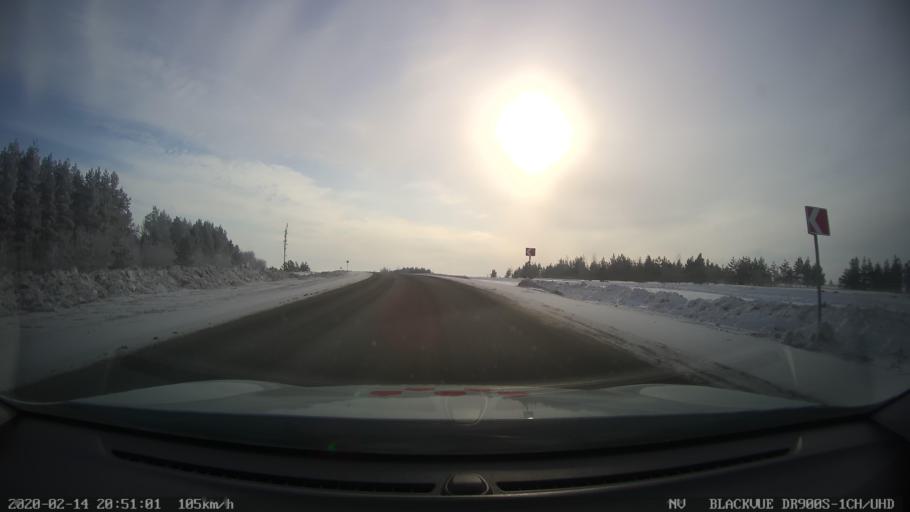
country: RU
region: Tatarstan
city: Kuybyshevskiy Zaton
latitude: 55.2180
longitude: 49.2318
